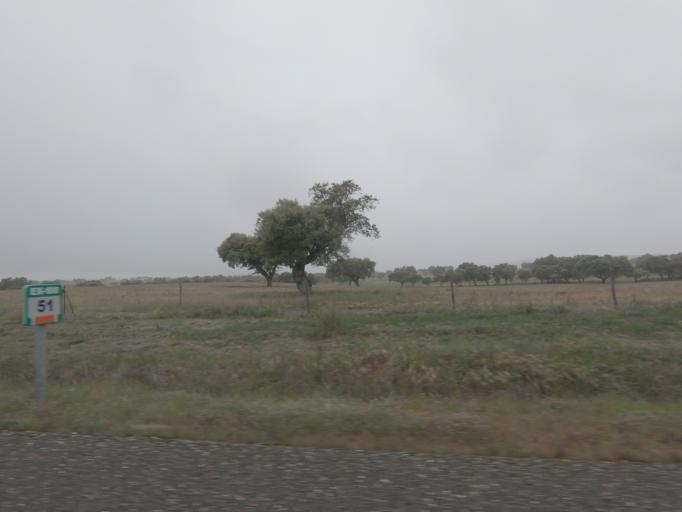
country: ES
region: Extremadura
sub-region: Provincia de Badajoz
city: La Roca de la Sierra
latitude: 39.1050
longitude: -6.7101
